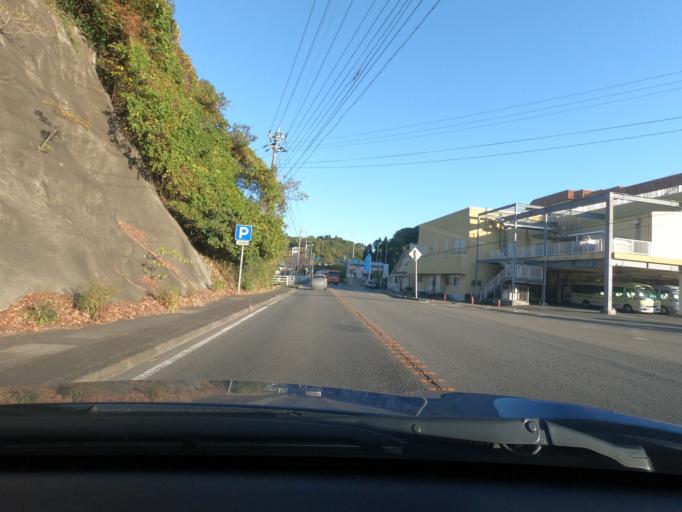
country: JP
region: Kagoshima
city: Satsumasendai
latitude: 31.8602
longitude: 130.2290
